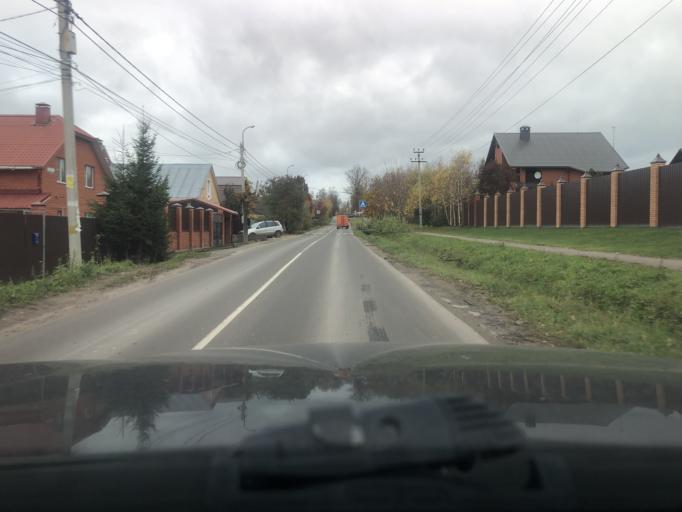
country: RU
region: Moskovskaya
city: Sergiyev Posad
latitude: 56.3037
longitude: 38.1098
